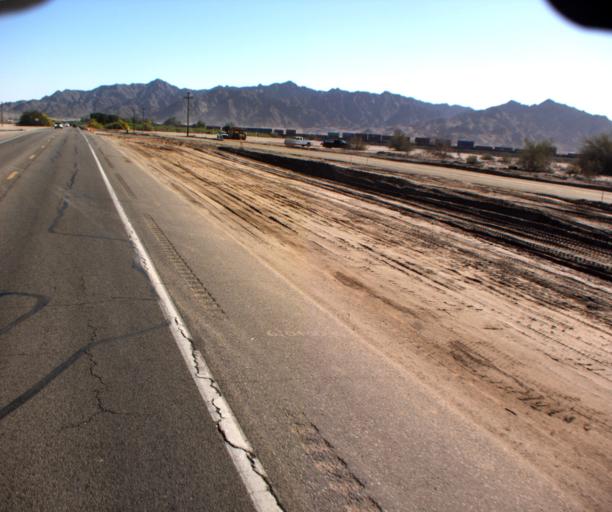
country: US
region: Arizona
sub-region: Yuma County
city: Fortuna Foothills
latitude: 32.7060
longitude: -114.4347
